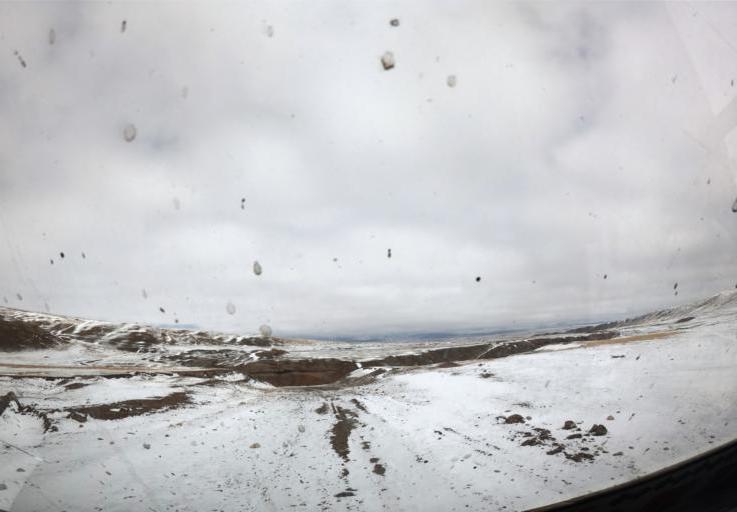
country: KG
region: Naryn
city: At-Bashi
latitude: 40.8070
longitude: 76.2644
